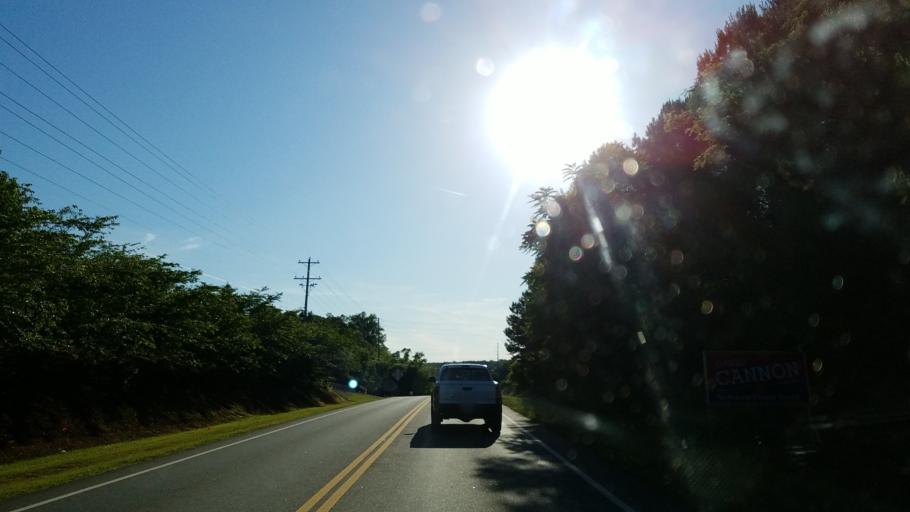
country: US
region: Georgia
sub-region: Cherokee County
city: Holly Springs
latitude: 34.1679
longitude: -84.4408
